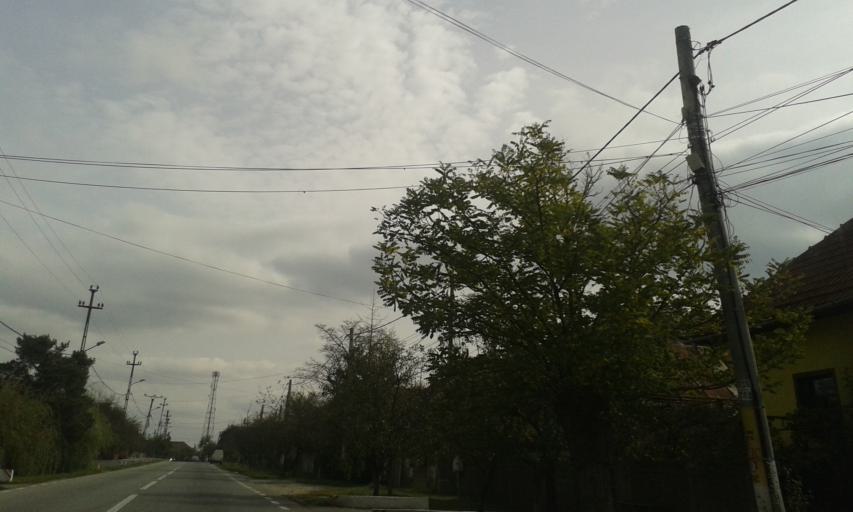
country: RO
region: Gorj
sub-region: Comuna Balanesti
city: Balanesti
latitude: 45.0425
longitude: 23.3478
